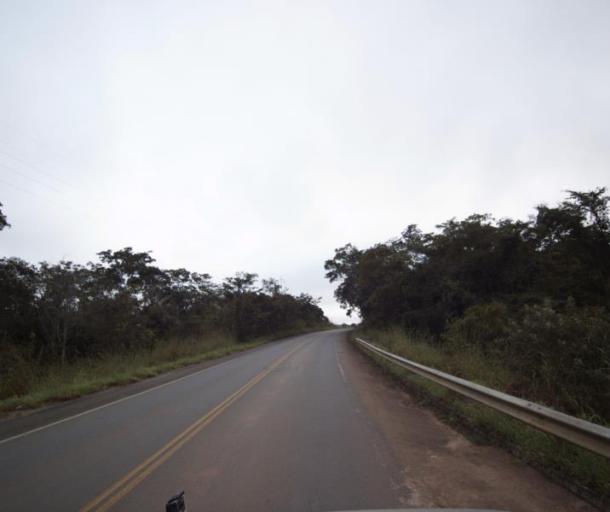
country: BR
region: Goias
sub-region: Pirenopolis
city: Pirenopolis
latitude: -15.8633
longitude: -48.7724
